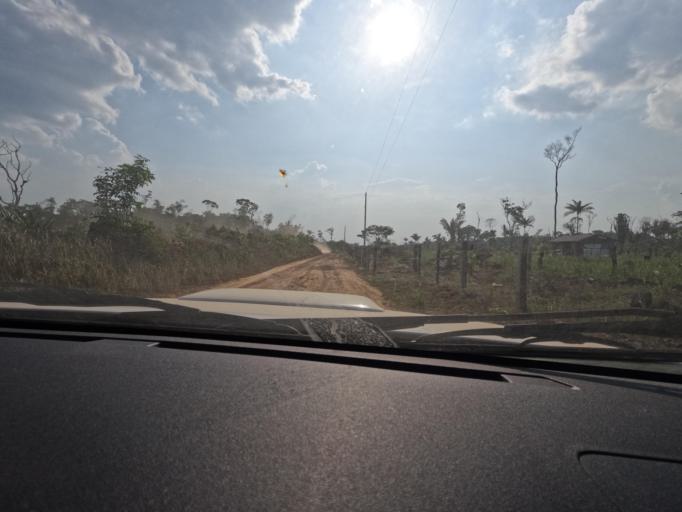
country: BR
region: Rondonia
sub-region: Porto Velho
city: Porto Velho
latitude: -8.5743
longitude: -63.9997
